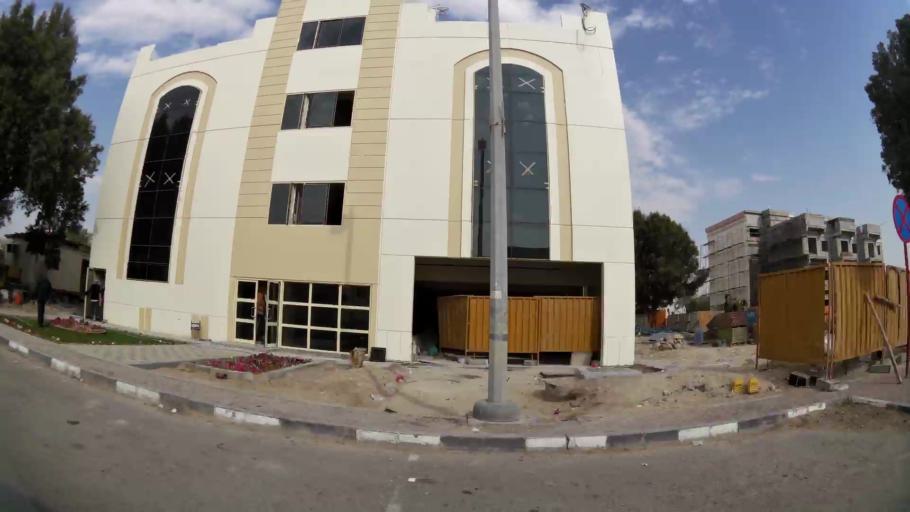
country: AE
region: Abu Dhabi
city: Abu Dhabi
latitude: 24.3195
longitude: 54.5310
